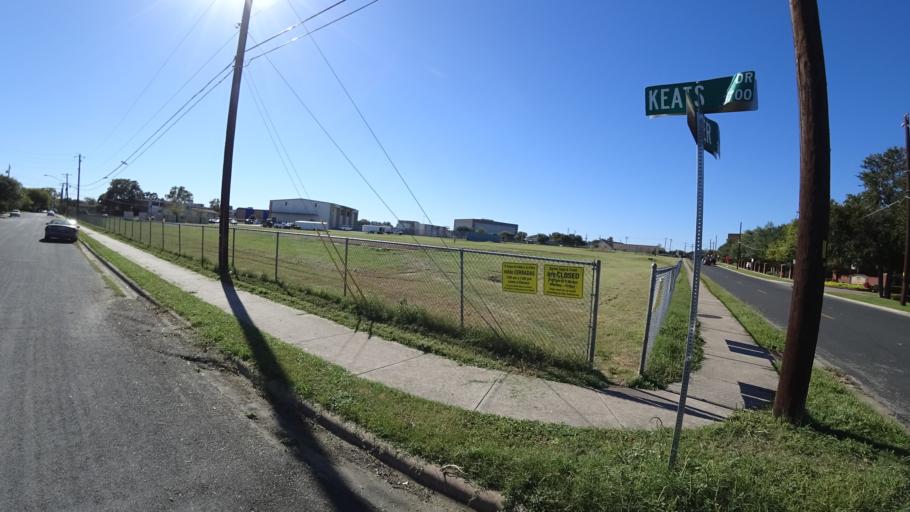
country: US
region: Texas
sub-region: Travis County
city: Rollingwood
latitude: 30.2372
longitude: -97.7866
